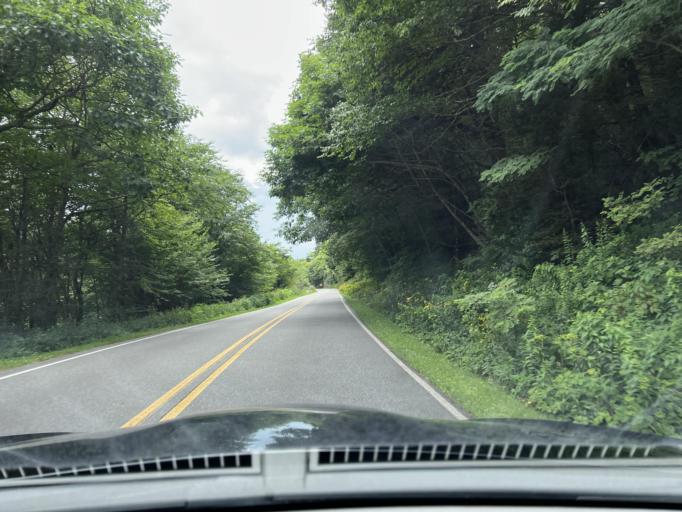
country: US
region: North Carolina
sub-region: Buncombe County
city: Black Mountain
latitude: 35.7209
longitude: -82.2798
